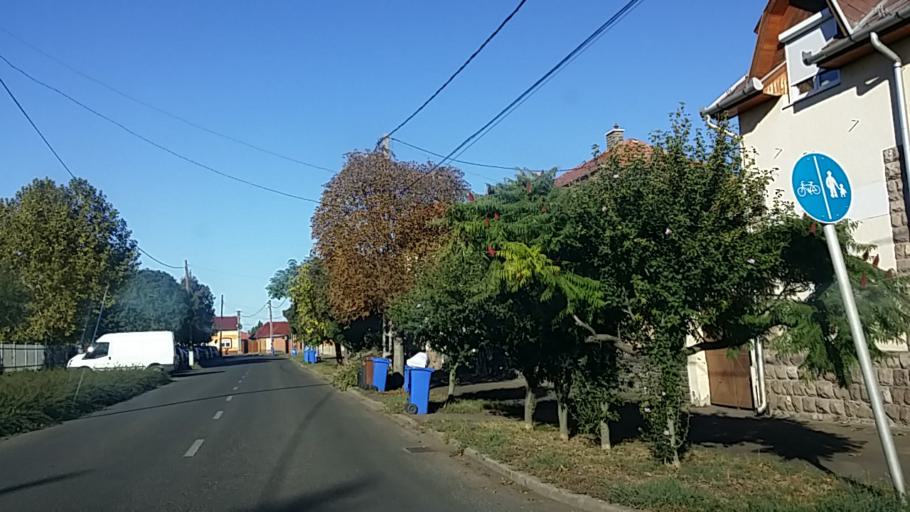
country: HU
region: Heves
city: Gyongyos
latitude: 47.7891
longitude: 19.9317
